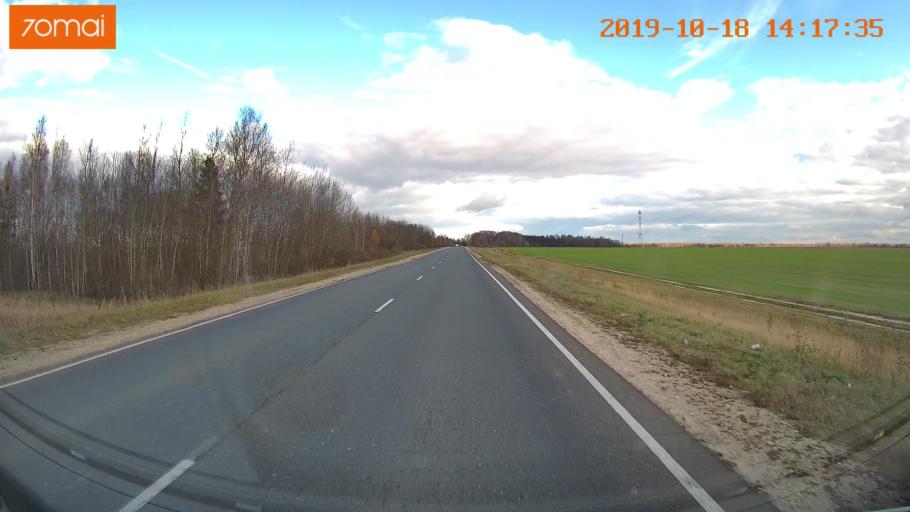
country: RU
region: Rjazan
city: Tuma
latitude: 55.1398
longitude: 40.3752
